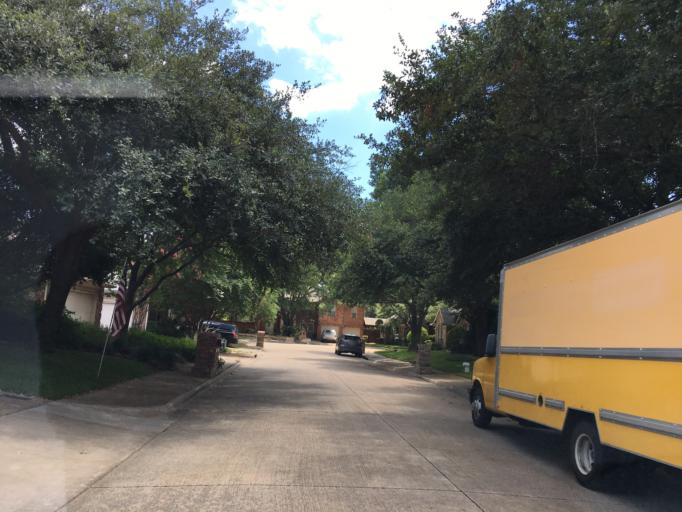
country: US
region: Texas
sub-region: Dallas County
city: Addison
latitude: 32.9447
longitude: -96.8443
